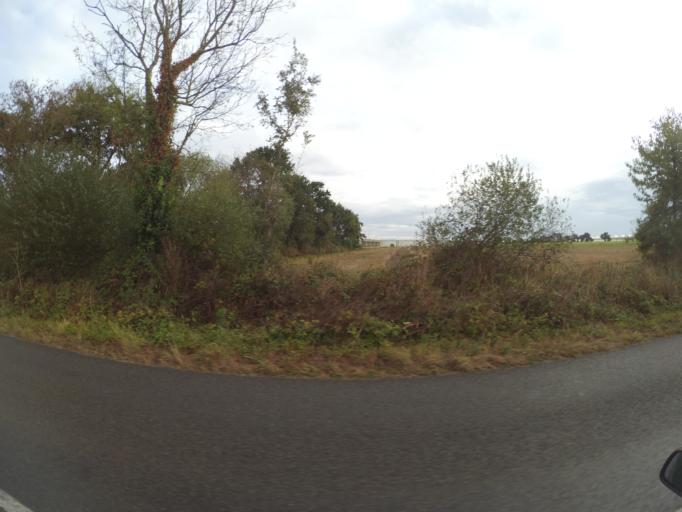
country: FR
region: Pays de la Loire
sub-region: Departement de la Loire-Atlantique
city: La Planche
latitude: 47.0242
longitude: -1.4525
